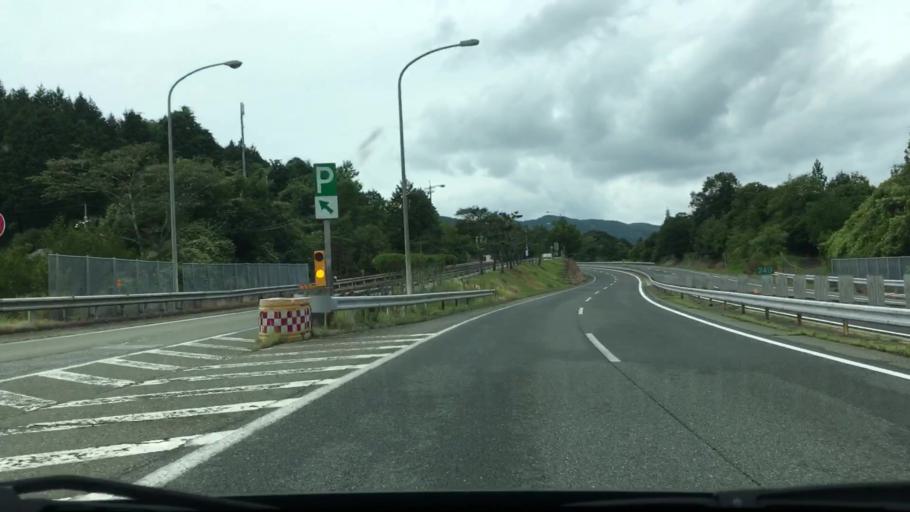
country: JP
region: Okayama
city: Niimi
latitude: 34.8928
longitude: 133.2569
